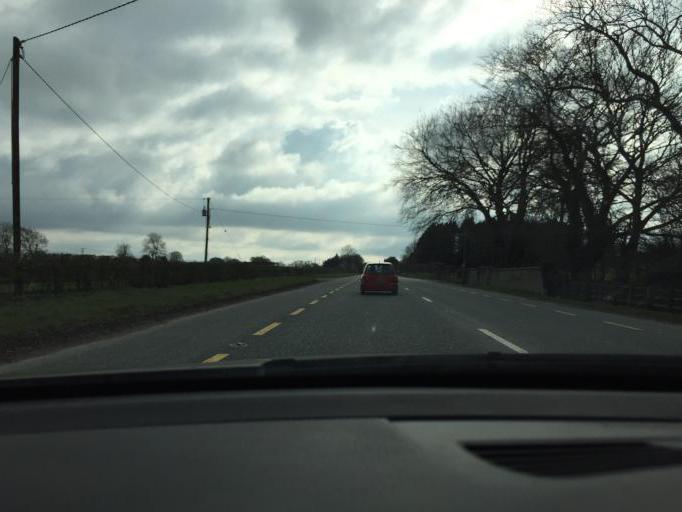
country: IE
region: Leinster
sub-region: Wicklow
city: Blessington
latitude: 53.1883
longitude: -6.5162
